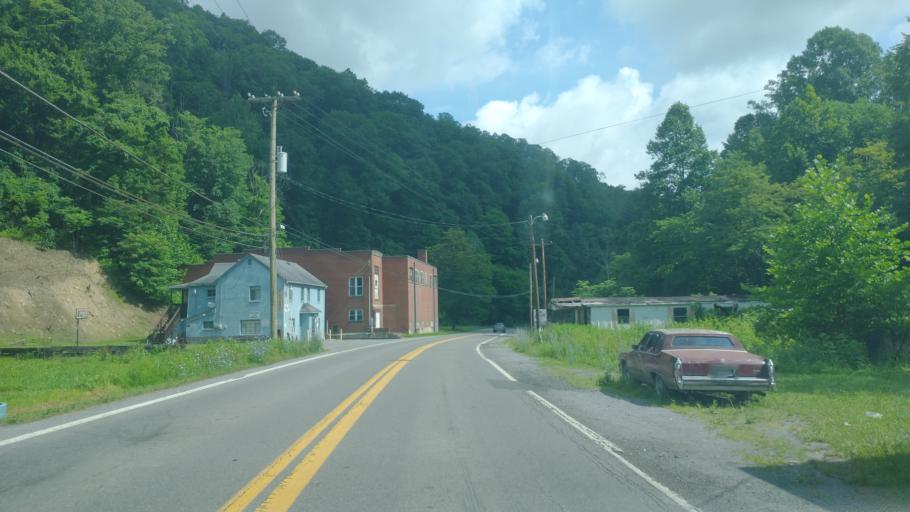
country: US
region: West Virginia
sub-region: McDowell County
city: Welch
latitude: 37.3963
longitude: -81.4225
